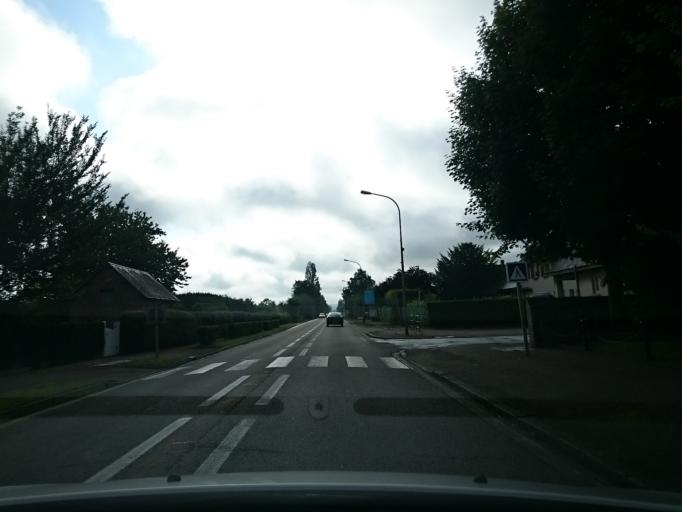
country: FR
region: Lower Normandy
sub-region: Departement du Calvados
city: Cambremer
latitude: 49.1182
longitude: 0.0178
